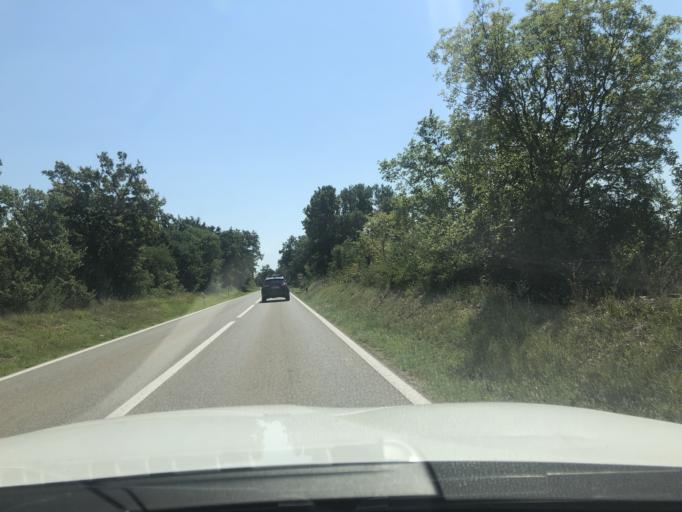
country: HR
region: Istarska
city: Vodnjan
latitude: 45.0191
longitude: 13.8035
